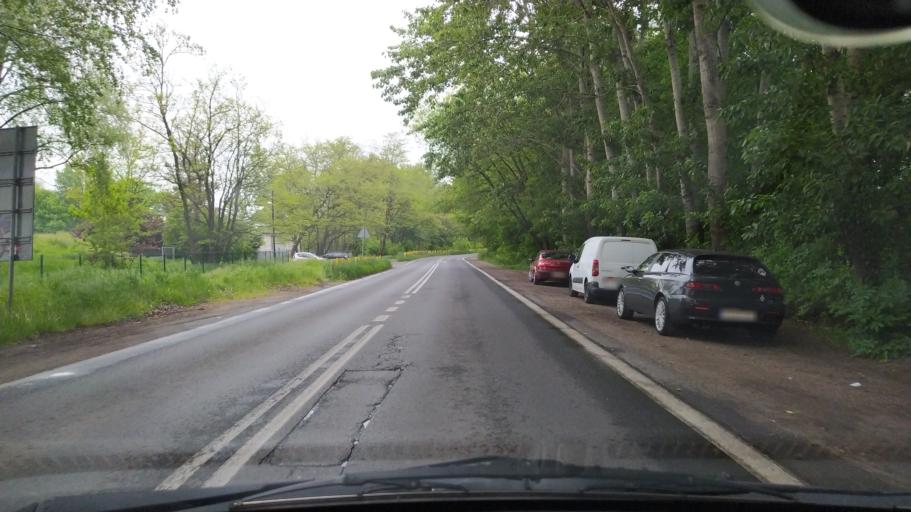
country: PL
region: Silesian Voivodeship
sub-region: Powiat gliwicki
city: Przyszowice
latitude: 50.2850
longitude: 18.7201
